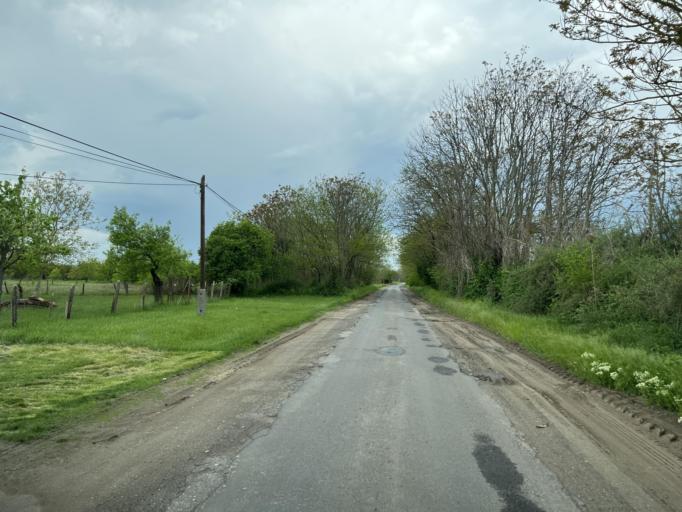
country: HU
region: Pest
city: Nagykoros
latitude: 47.0098
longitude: 19.7960
